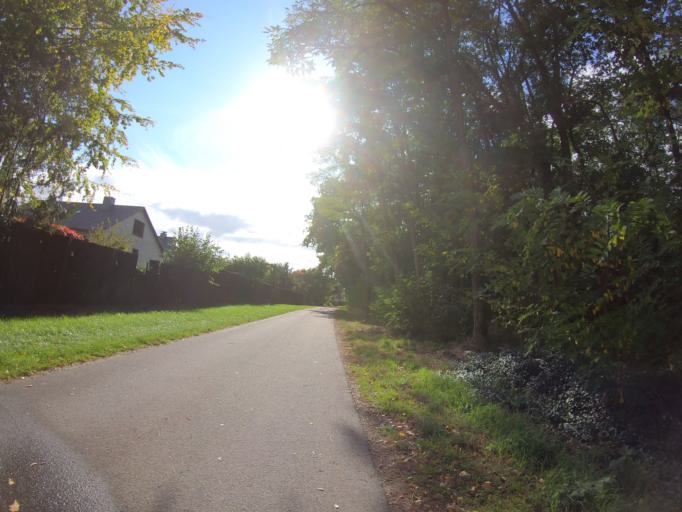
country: DE
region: Lower Saxony
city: Isenbuttel
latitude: 52.4439
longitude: 10.5723
